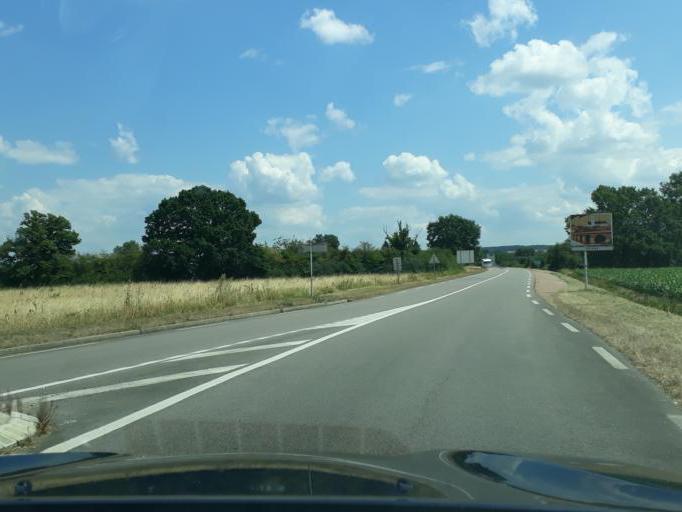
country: FR
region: Bourgogne
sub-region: Departement de la Nievre
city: Challuy
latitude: 46.9580
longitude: 3.1511
